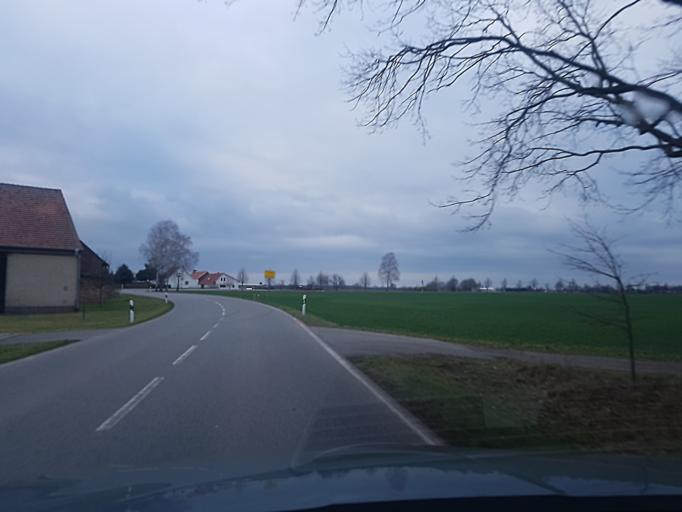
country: DE
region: Brandenburg
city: Sonnewalde
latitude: 51.6771
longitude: 13.6867
